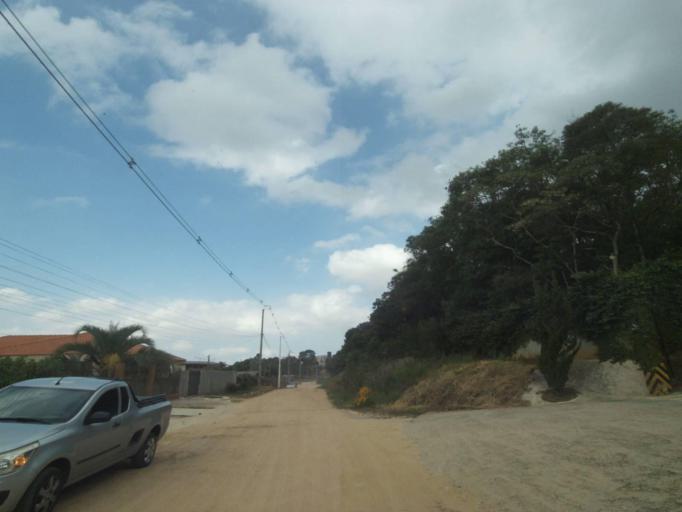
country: BR
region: Parana
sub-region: Araucaria
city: Araucaria
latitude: -25.5168
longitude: -49.3459
